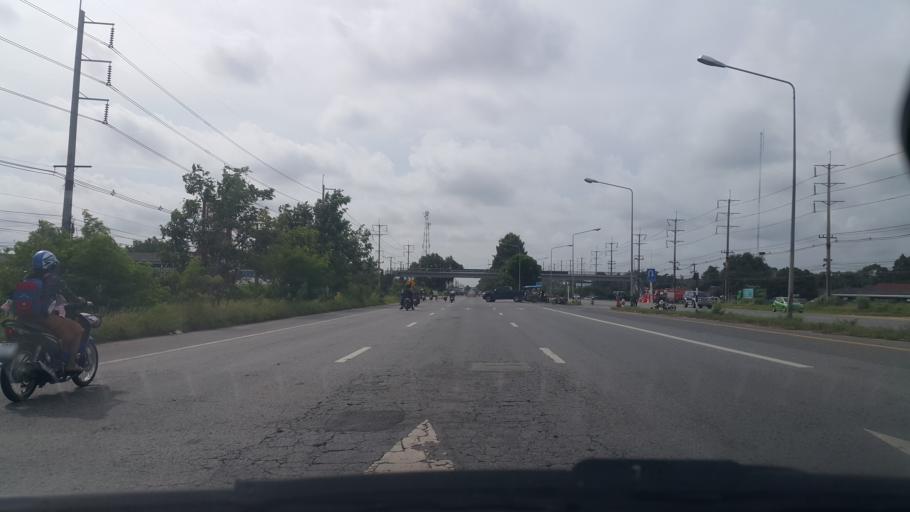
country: TH
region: Rayong
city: Rayong
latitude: 12.6727
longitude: 101.3047
